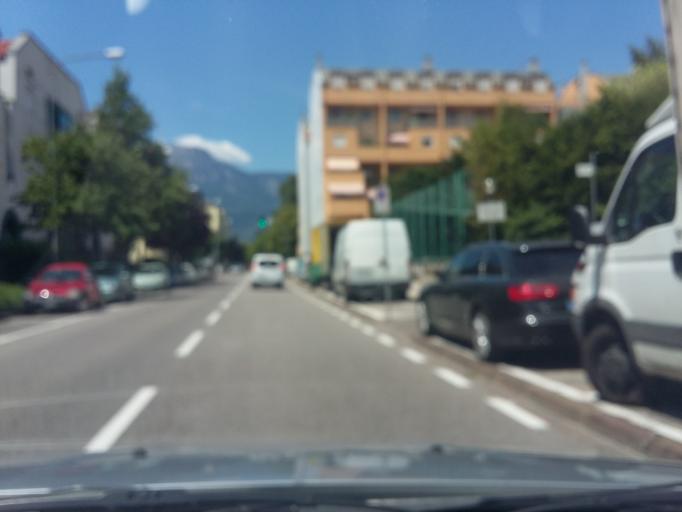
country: IT
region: Trentino-Alto Adige
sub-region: Bolzano
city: Bolzano
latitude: 46.4884
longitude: 11.3286
